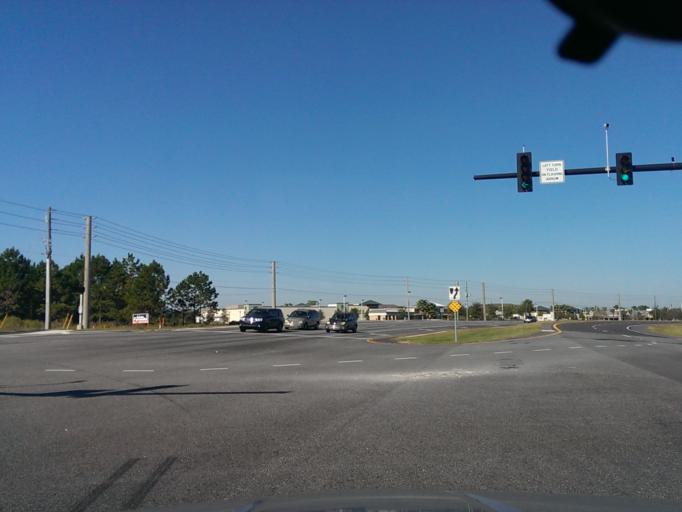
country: US
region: Florida
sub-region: Orange County
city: Bay Hill
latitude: 28.4464
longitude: -81.5581
